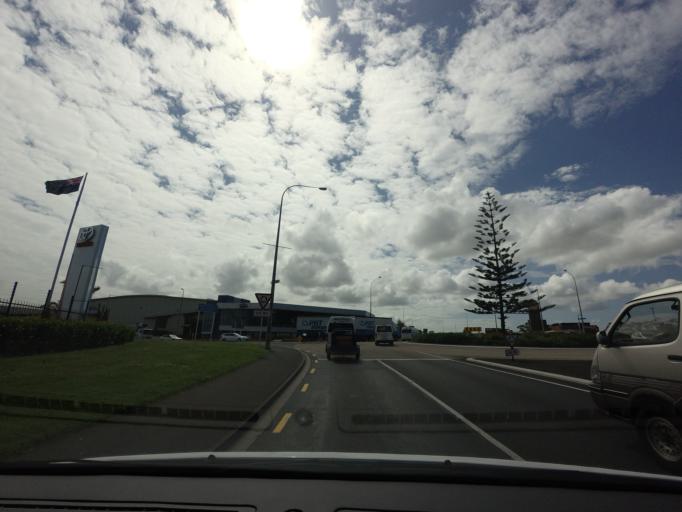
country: NZ
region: Auckland
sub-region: Auckland
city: Mangere
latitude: -36.9989
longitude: 174.7876
